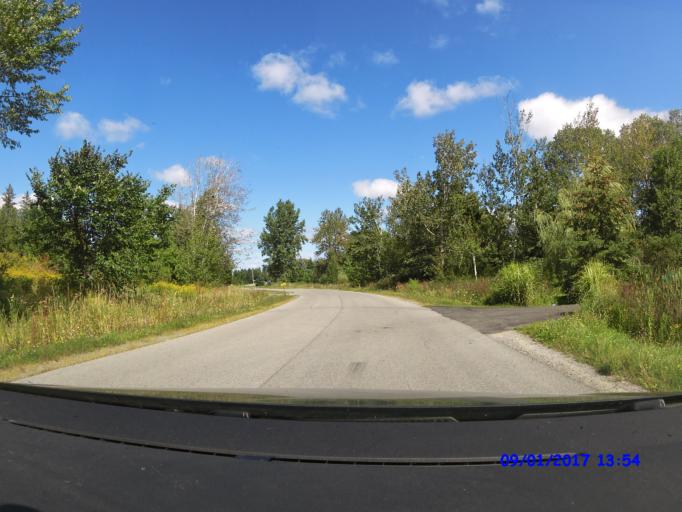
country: CA
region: Ontario
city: Bells Corners
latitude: 45.3598
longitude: -75.9561
